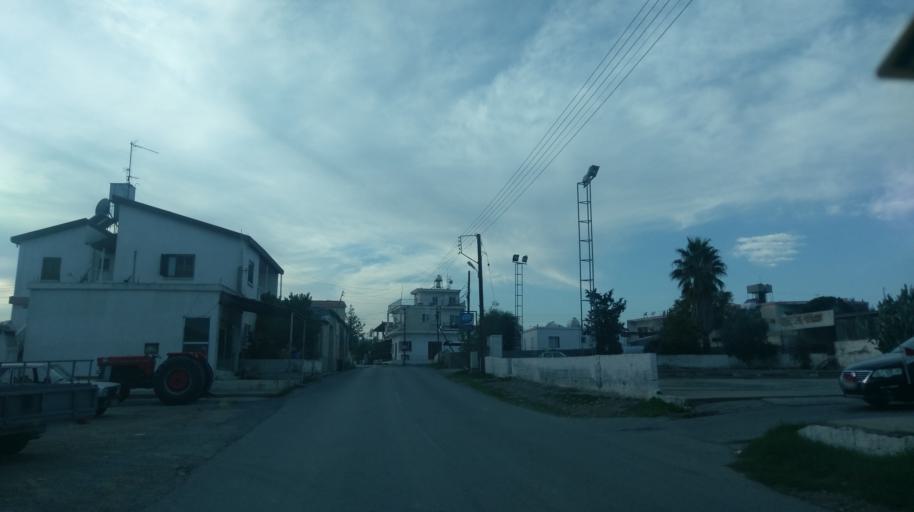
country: CY
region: Larnaka
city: Athienou
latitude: 35.1585
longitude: 33.5872
